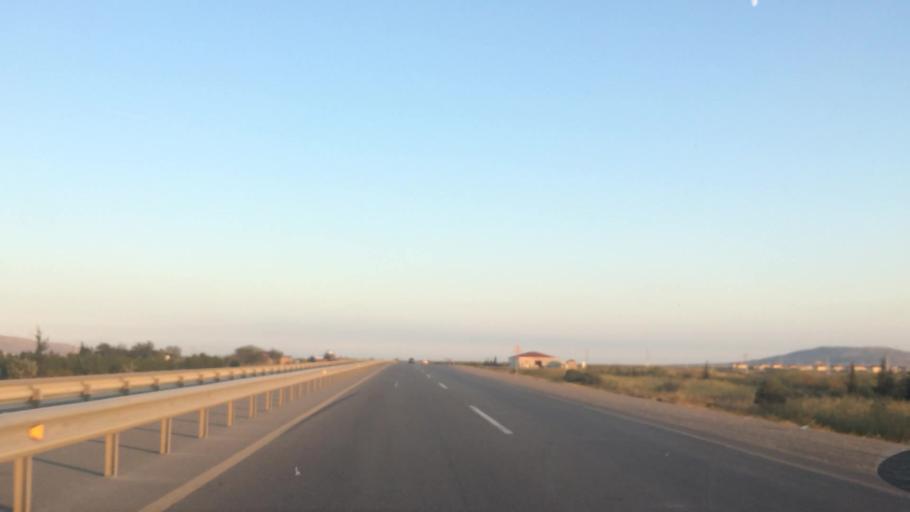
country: AZ
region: Baki
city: Qobustan
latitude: 39.9863
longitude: 49.2078
